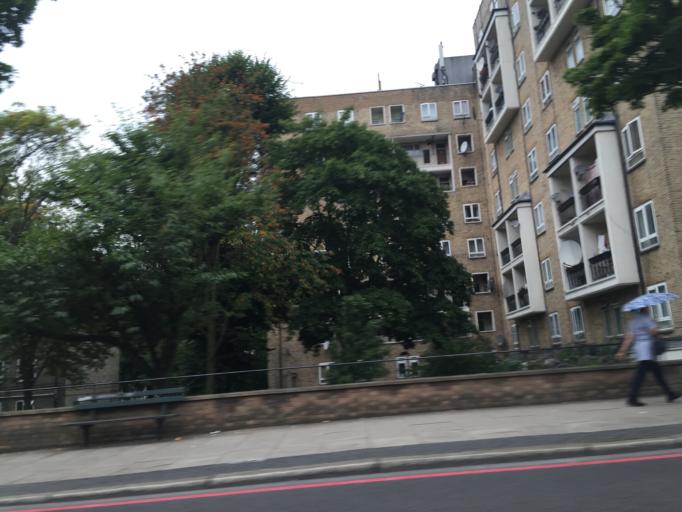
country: GB
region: England
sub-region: Greater London
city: Belsize Park
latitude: 51.5407
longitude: -0.1756
